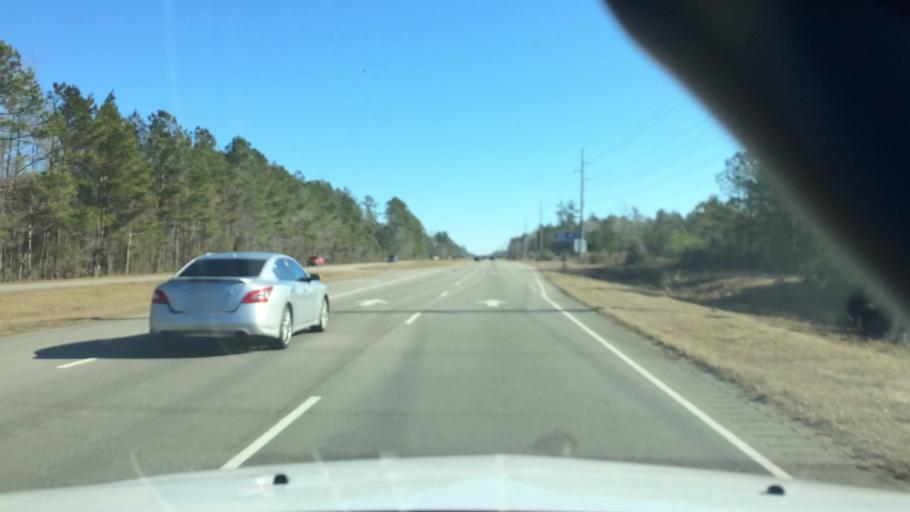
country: US
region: North Carolina
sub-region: Brunswick County
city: Shallotte
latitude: 34.0013
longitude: -78.3182
